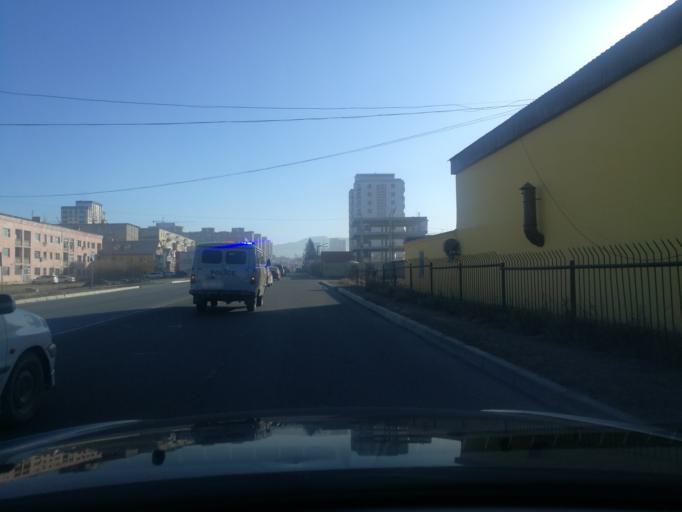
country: MN
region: Ulaanbaatar
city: Ulaanbaatar
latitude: 47.8559
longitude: 106.7567
